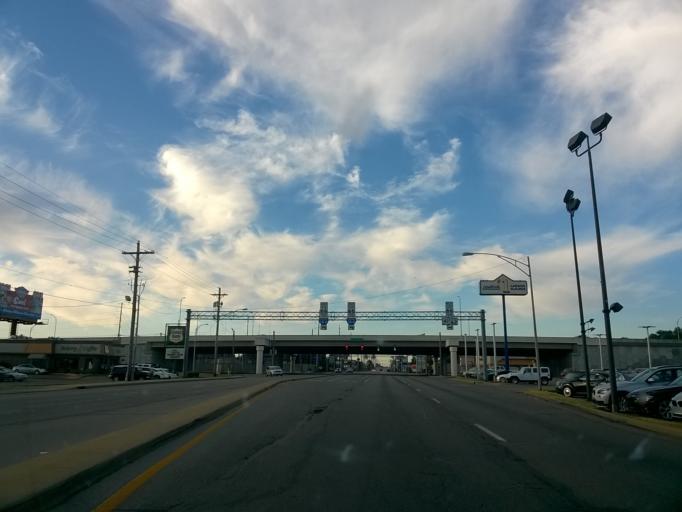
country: US
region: Indiana
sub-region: Vanderburgh County
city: Melody Hill
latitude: 37.9777
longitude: -87.4926
